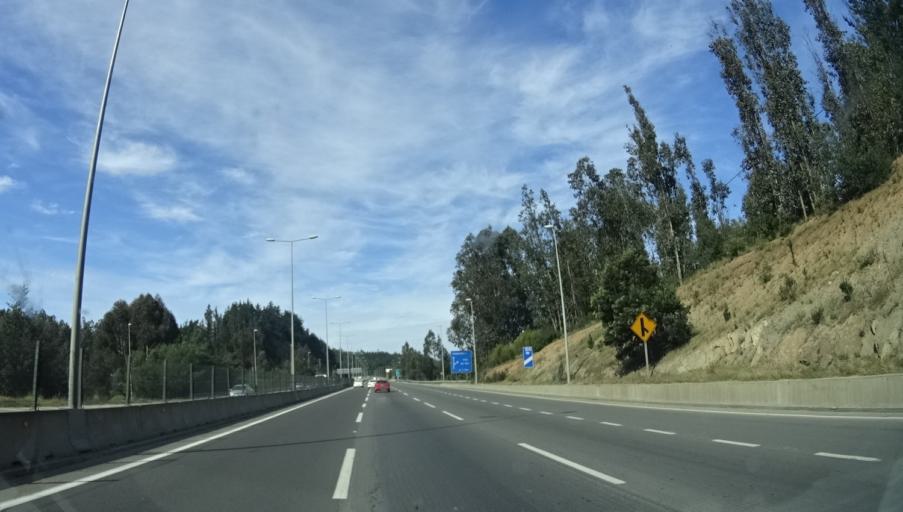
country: CL
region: Valparaiso
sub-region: Provincia de Valparaiso
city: Vina del Mar
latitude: -33.1093
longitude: -71.5575
